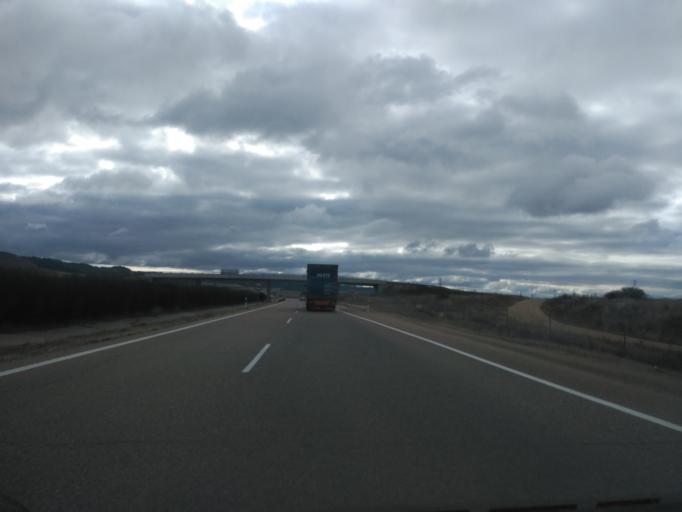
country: ES
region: Castille and Leon
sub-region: Provincia de Palencia
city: Fuentes de Valdepero
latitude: 42.0579
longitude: -4.4928
